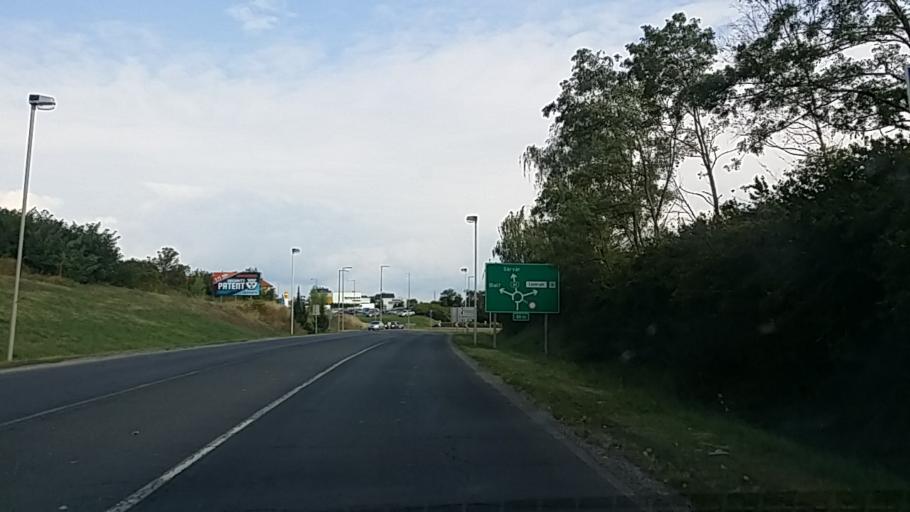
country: HU
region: Gyor-Moson-Sopron
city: Sopron
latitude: 47.6832
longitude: 16.6122
